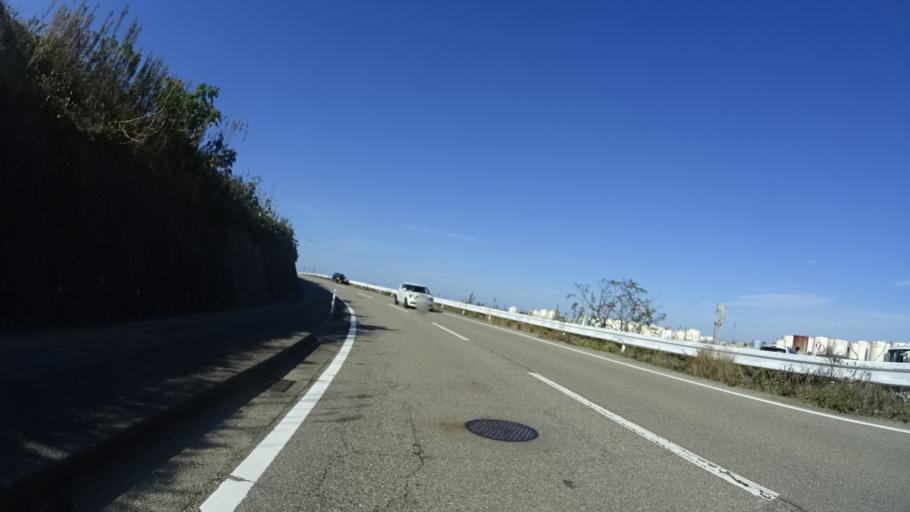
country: JP
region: Ishikawa
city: Kanazawa-shi
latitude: 36.6151
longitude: 136.6087
